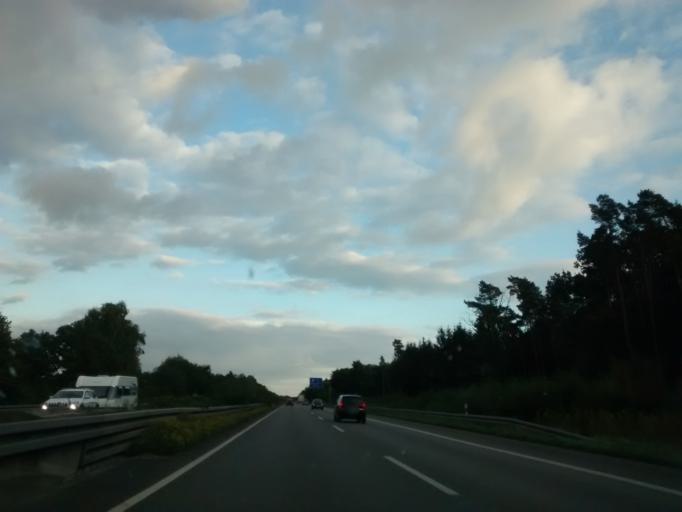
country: DE
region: North Rhine-Westphalia
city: Ibbenburen
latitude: 52.2624
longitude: 7.6885
